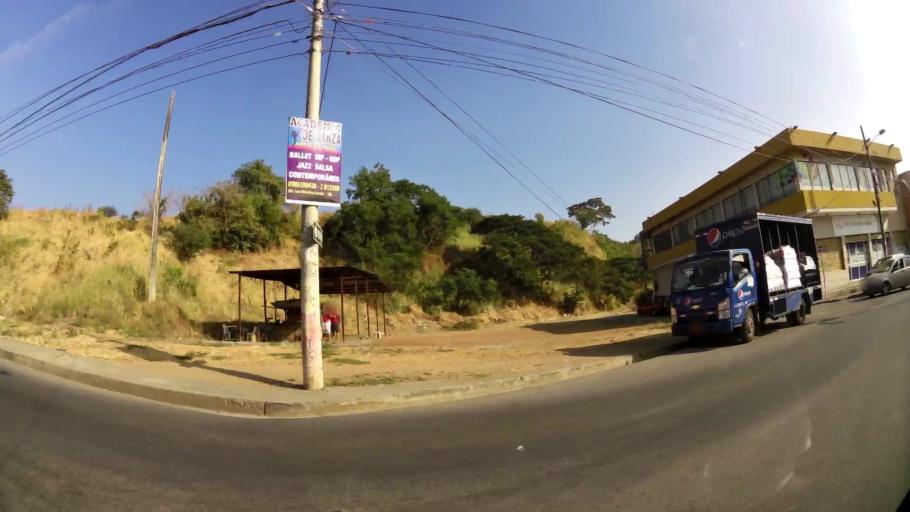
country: EC
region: Guayas
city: Eloy Alfaro
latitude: -2.1771
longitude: -79.8494
